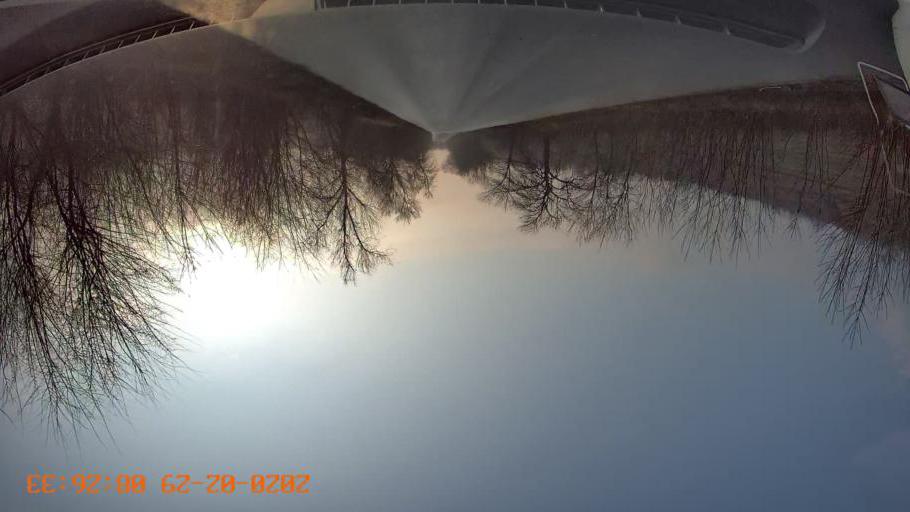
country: MD
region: Anenii Noi
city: Anenii Noi
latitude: 46.8882
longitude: 29.2616
